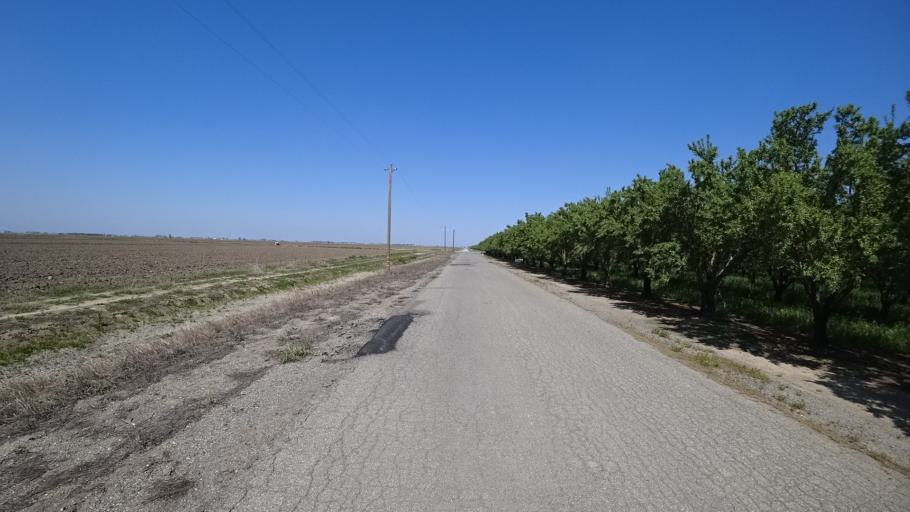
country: US
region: California
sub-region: Glenn County
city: Willows
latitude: 39.5347
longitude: -122.0279
